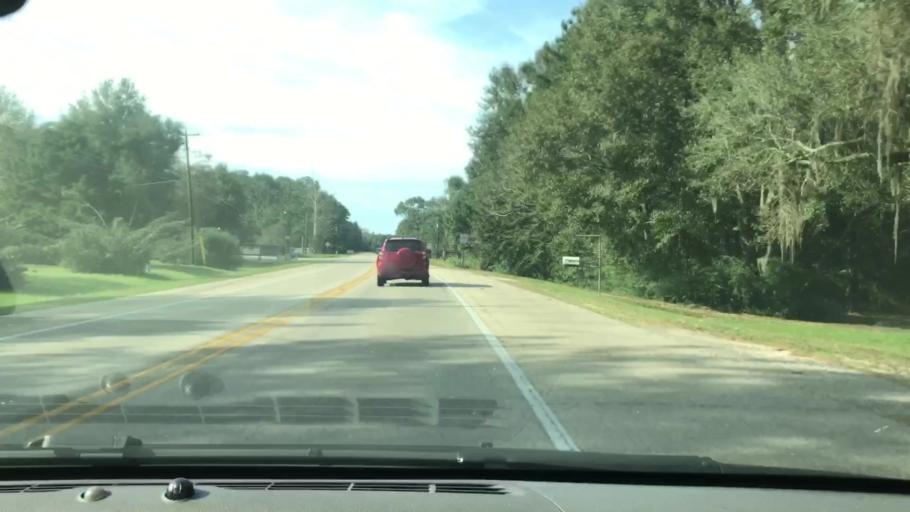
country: US
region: Louisiana
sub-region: Saint Tammany Parish
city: Pearl River
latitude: 30.4594
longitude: -89.8048
